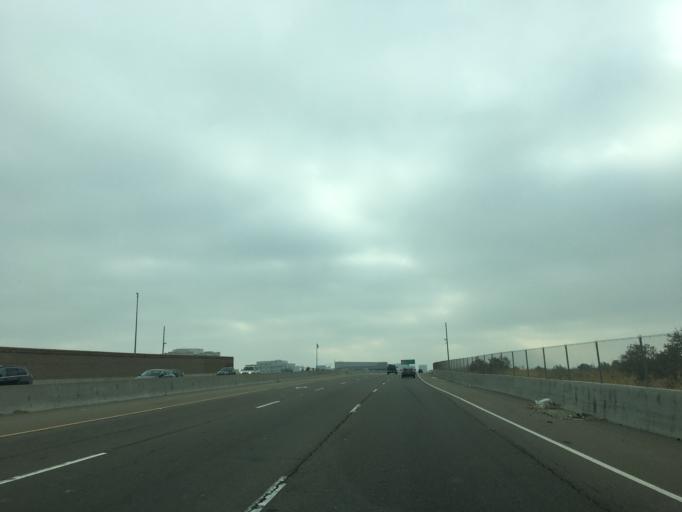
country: US
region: California
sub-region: Santa Clara County
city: San Jose
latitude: 37.3554
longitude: -121.9125
